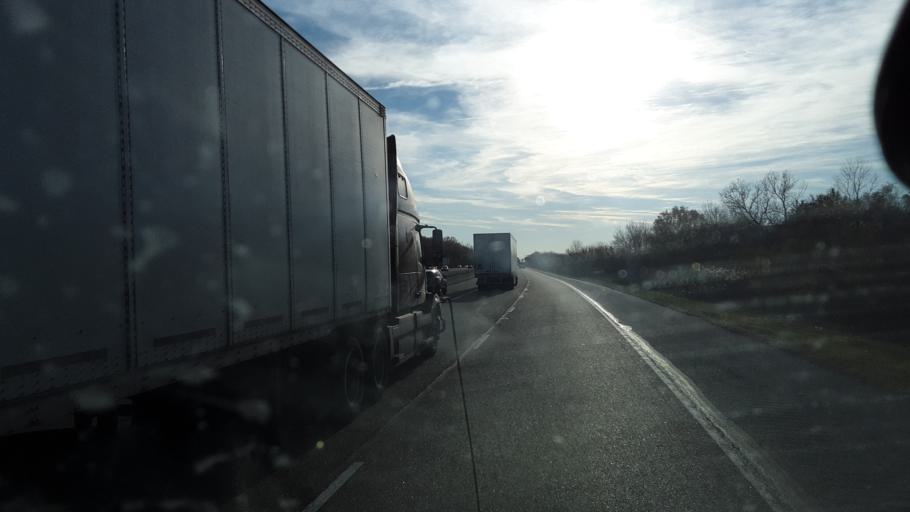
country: US
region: Illinois
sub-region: Saint Clair County
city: Fairmont City
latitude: 38.6604
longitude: -90.1063
